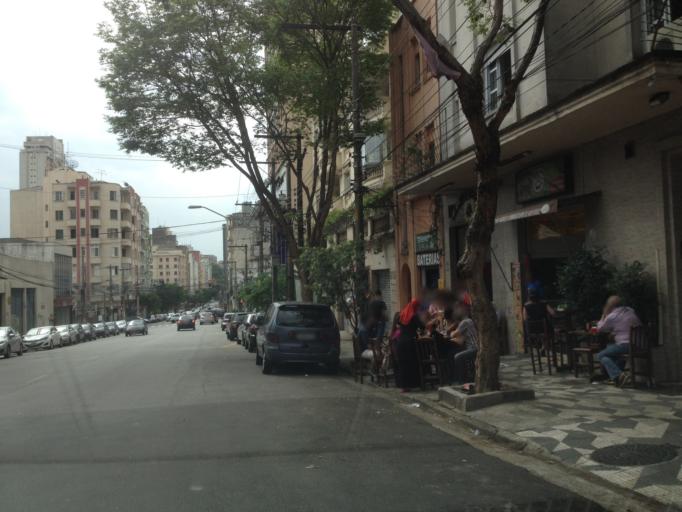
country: BR
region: Sao Paulo
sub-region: Sao Paulo
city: Sao Paulo
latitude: -23.5359
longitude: -46.6464
